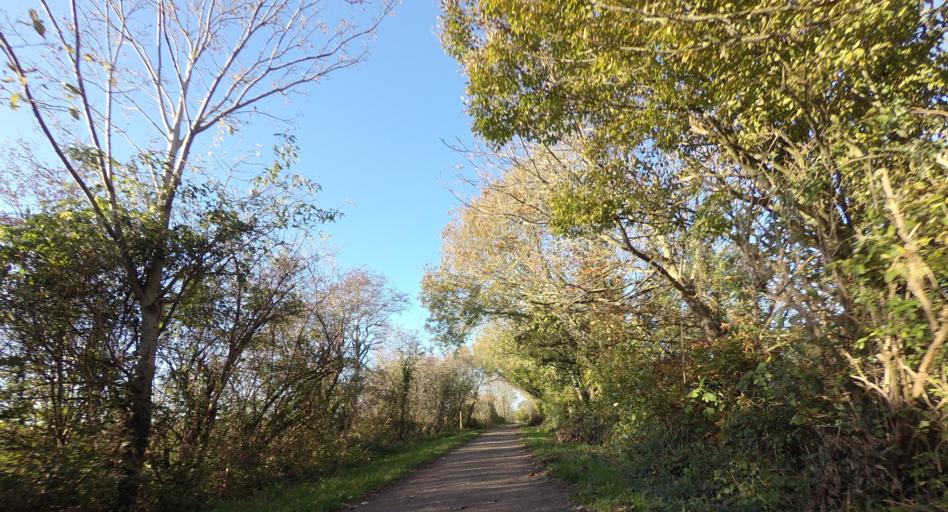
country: GB
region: England
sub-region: West Sussex
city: Steyning
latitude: 50.8637
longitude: -0.2998
